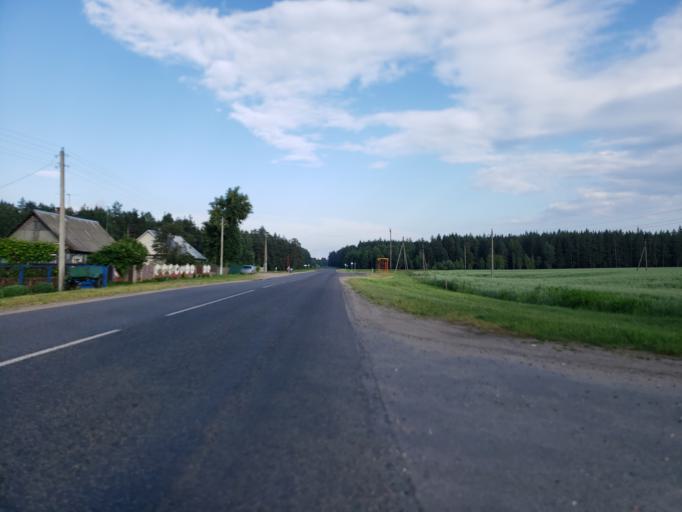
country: BY
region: Minsk
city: Chervyen'
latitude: 53.6968
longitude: 28.4529
